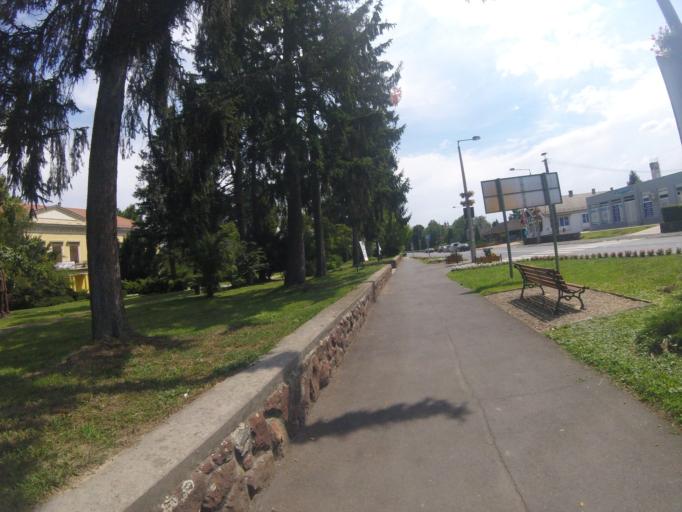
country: HU
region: Zala
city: Letenye
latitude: 46.4338
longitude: 16.7229
